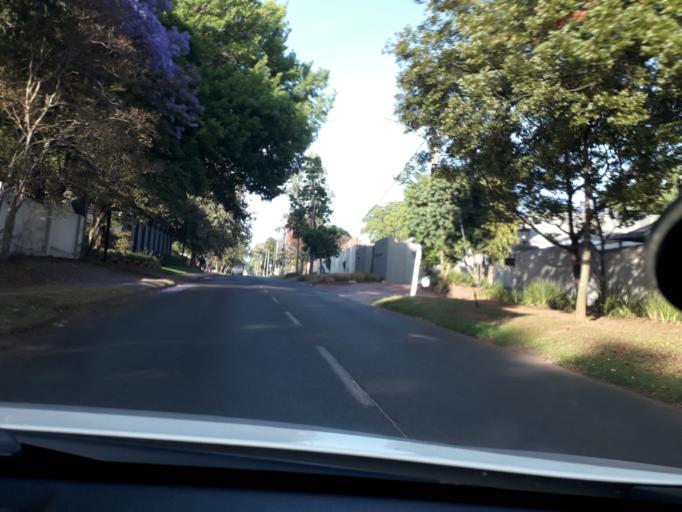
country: ZA
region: Gauteng
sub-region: City of Johannesburg Metropolitan Municipality
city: Johannesburg
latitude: -26.1231
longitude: 28.0587
